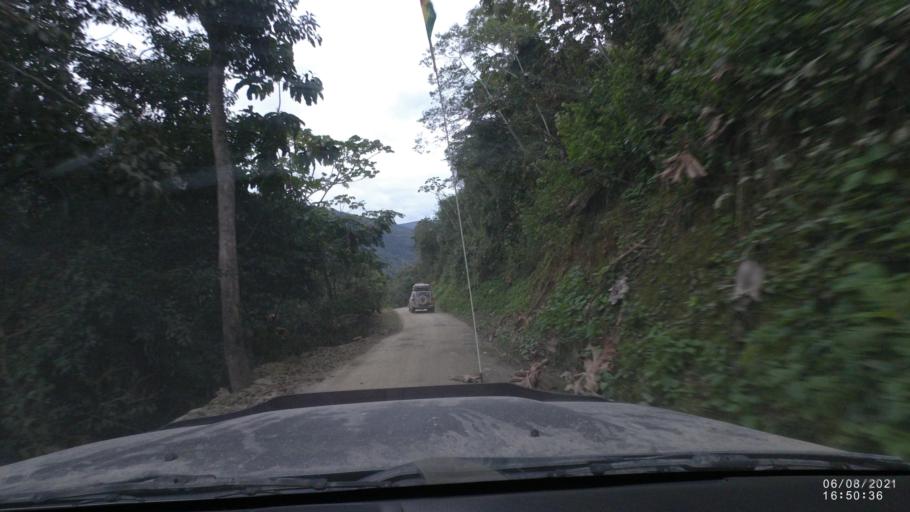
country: BO
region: La Paz
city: Quime
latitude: -16.4987
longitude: -66.7721
